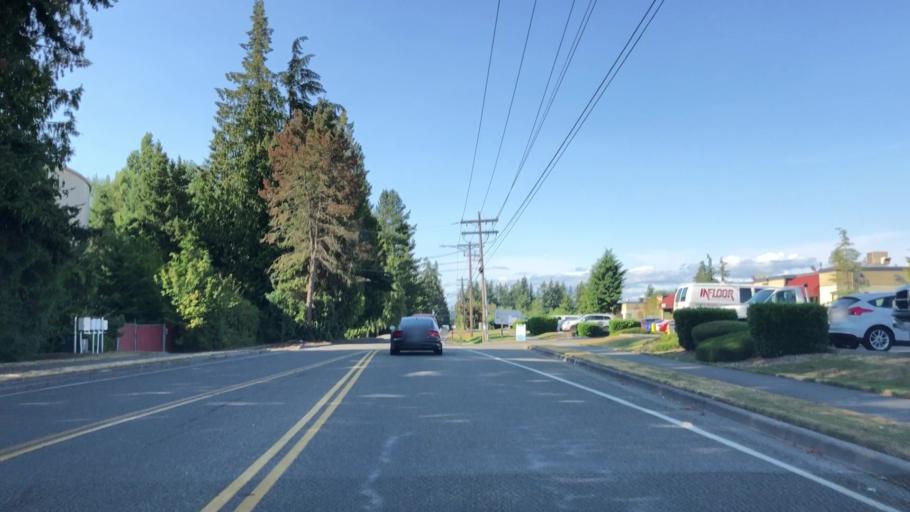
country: US
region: Washington
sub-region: Snohomish County
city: Mukilteo
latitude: 47.9226
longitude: -122.2932
